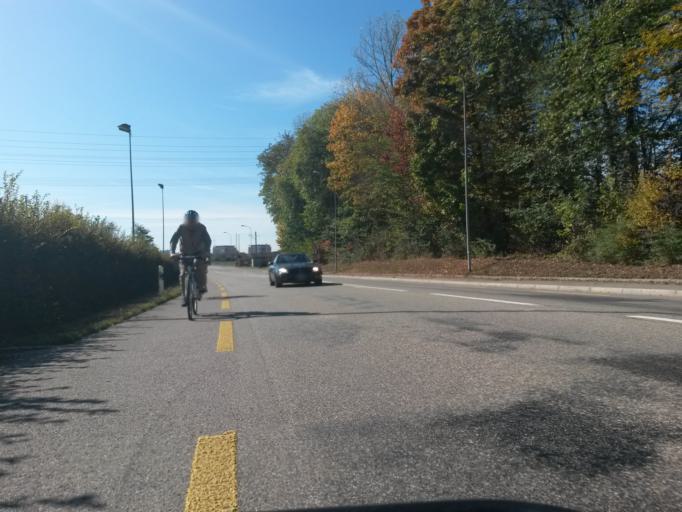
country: CH
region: Solothurn
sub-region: Bezirk Wasseramt
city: Luterbach
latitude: 47.2138
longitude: 7.5720
